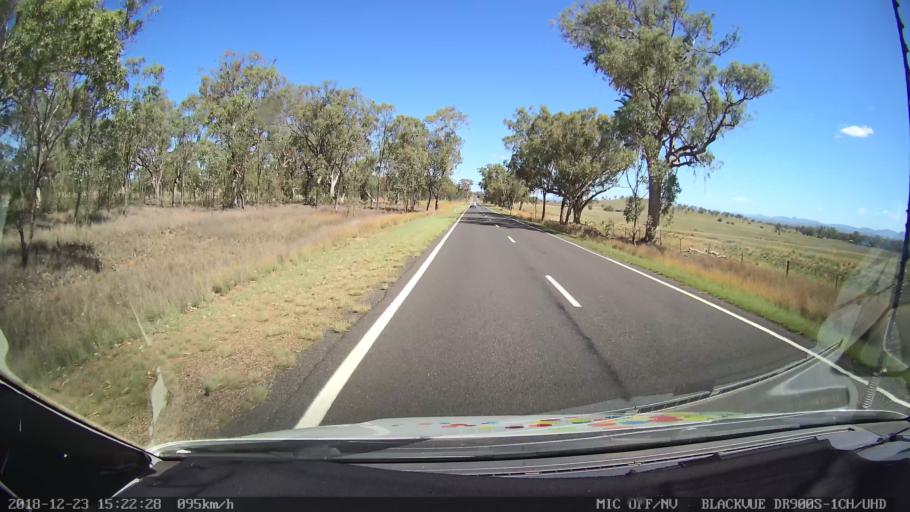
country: AU
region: New South Wales
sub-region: Tamworth Municipality
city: Manilla
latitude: -30.8687
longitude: 150.8052
